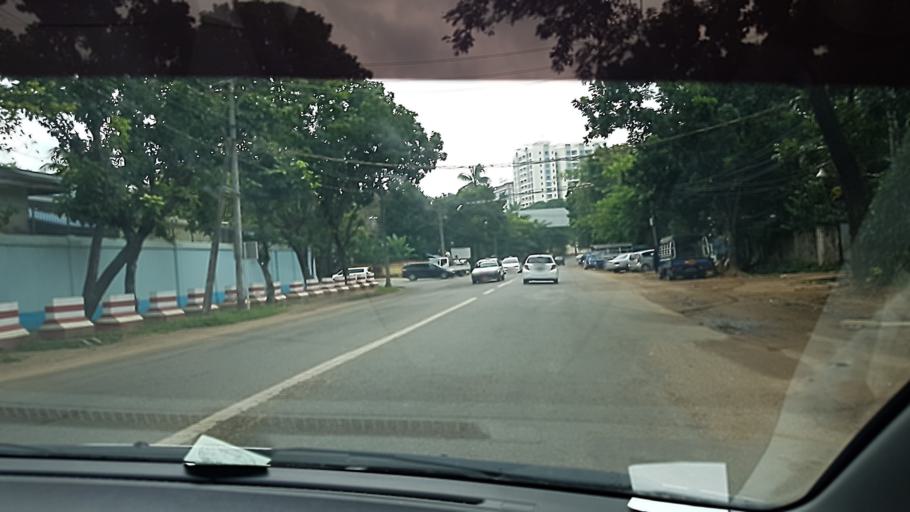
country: MM
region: Yangon
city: Yangon
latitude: 16.7886
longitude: 96.1338
